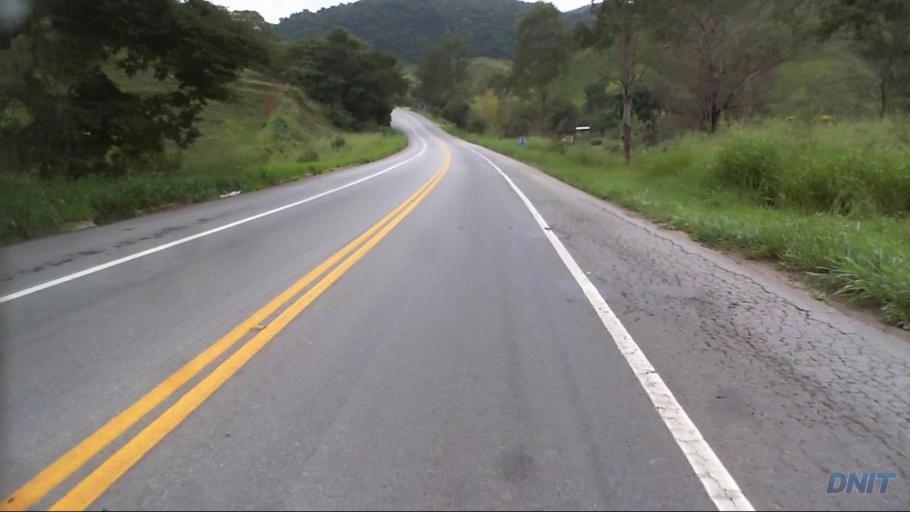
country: BR
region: Minas Gerais
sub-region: Timoteo
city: Timoteo
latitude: -19.6297
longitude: -42.8333
